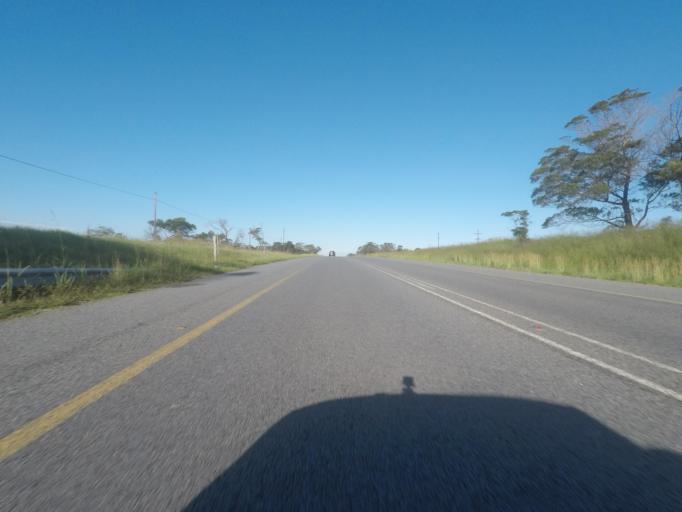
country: ZA
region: Eastern Cape
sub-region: Buffalo City Metropolitan Municipality
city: East London
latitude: -33.0574
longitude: 27.7969
